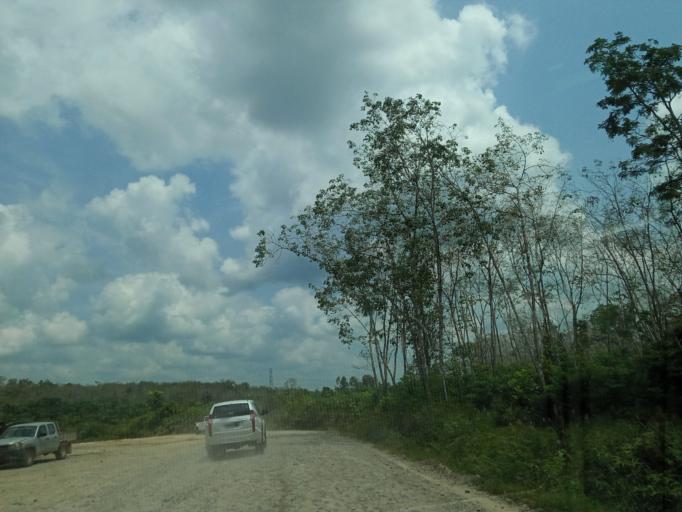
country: ID
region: Jambi
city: Mersam
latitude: -1.6487
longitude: 102.9454
